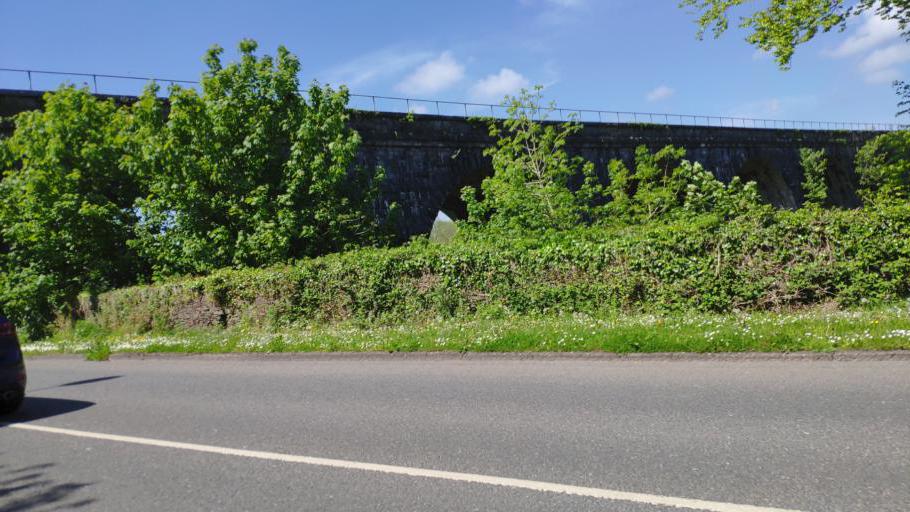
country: IE
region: Munster
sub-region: County Cork
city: Cork
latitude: 51.9265
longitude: -8.4867
